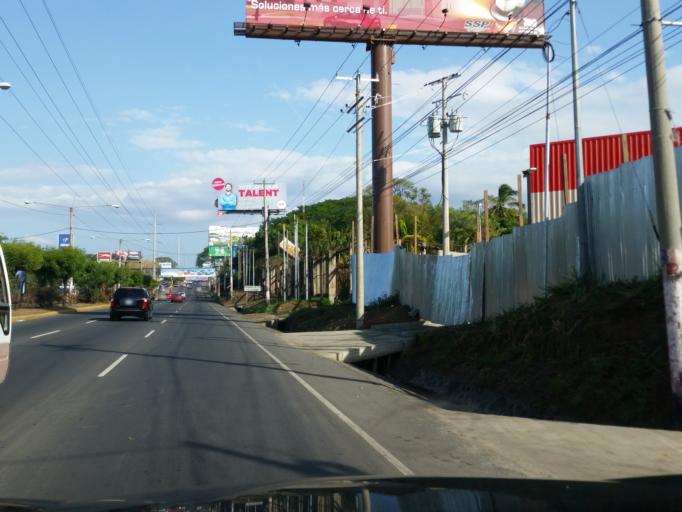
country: NI
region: Managua
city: Managua
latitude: 12.0996
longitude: -86.2430
